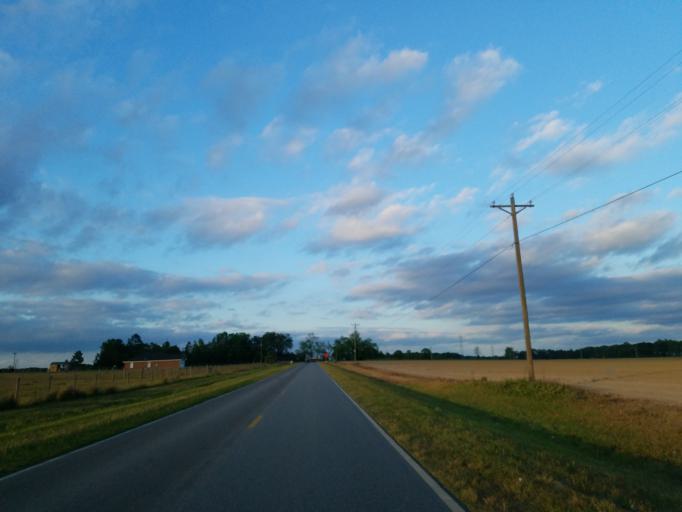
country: US
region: Georgia
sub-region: Lowndes County
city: Hahira
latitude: 31.0685
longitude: -83.3618
